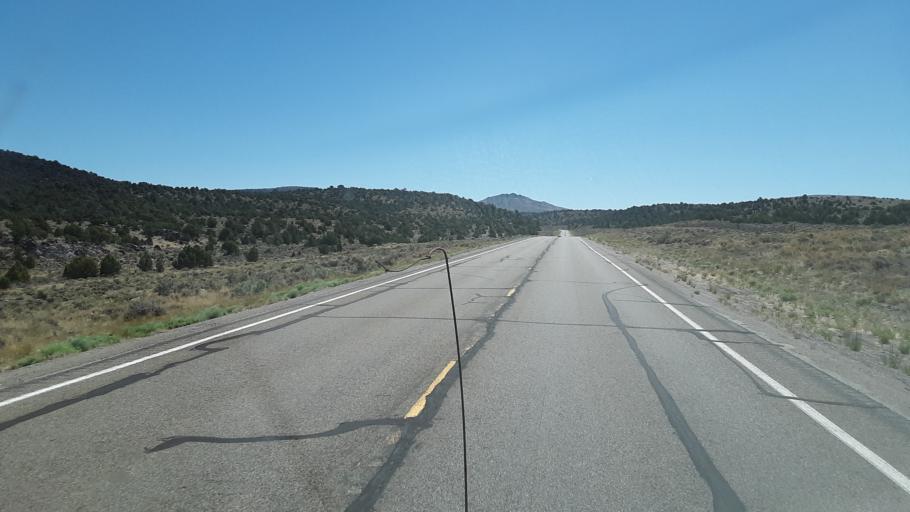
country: US
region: Nevada
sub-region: White Pine County
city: Ely
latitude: 39.4281
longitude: -115.1652
